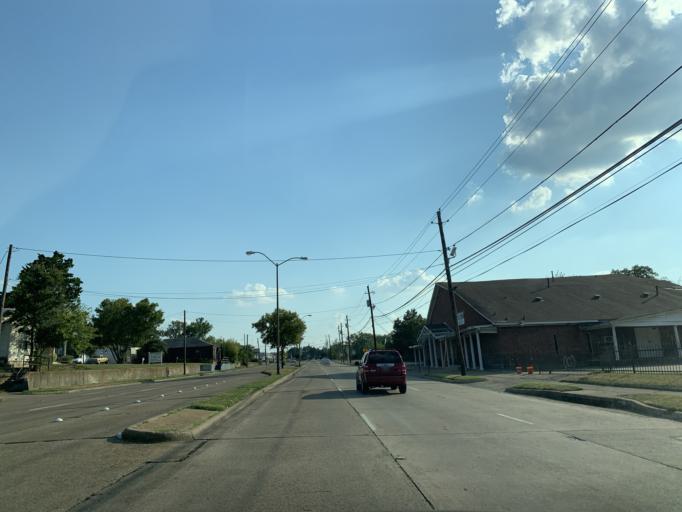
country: US
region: Texas
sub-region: Dallas County
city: Dallas
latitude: 32.7345
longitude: -96.7924
